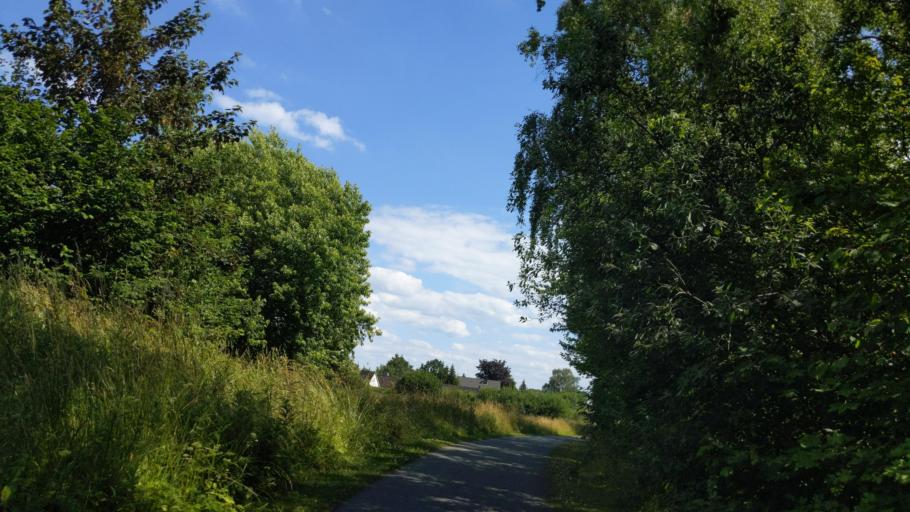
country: DE
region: Schleswig-Holstein
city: Gromitz
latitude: 54.1525
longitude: 10.9465
